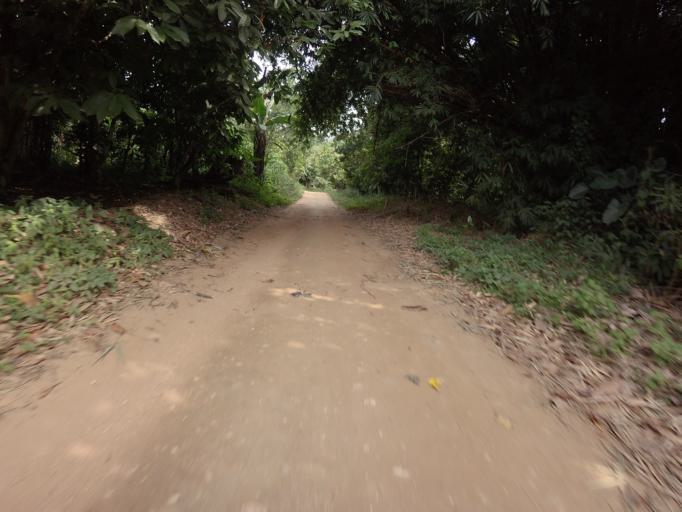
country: GH
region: Volta
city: Kpandu
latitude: 6.8846
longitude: 0.4371
